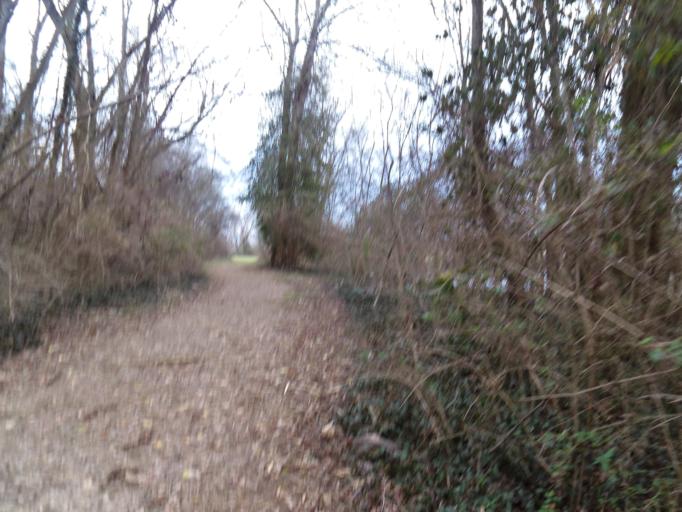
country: US
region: Tennessee
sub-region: Knox County
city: Knoxville
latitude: 35.9312
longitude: -83.9573
